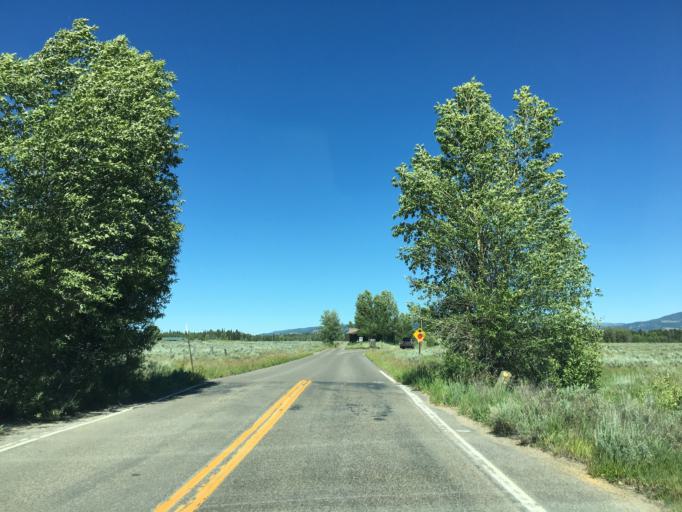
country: US
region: Wyoming
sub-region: Teton County
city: Moose Wilson Road
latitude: 43.5964
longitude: -110.8050
